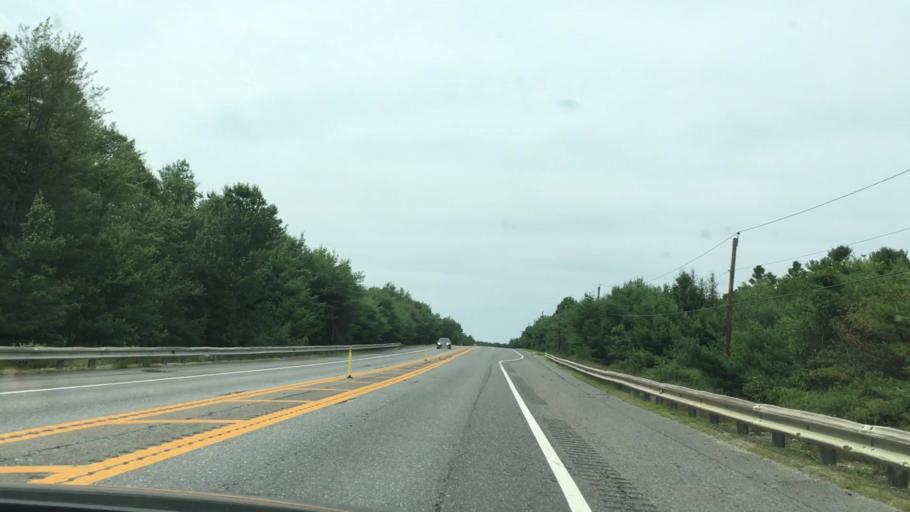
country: US
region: Massachusetts
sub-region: Worcester County
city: Gardner
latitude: 42.6098
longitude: -71.9973
